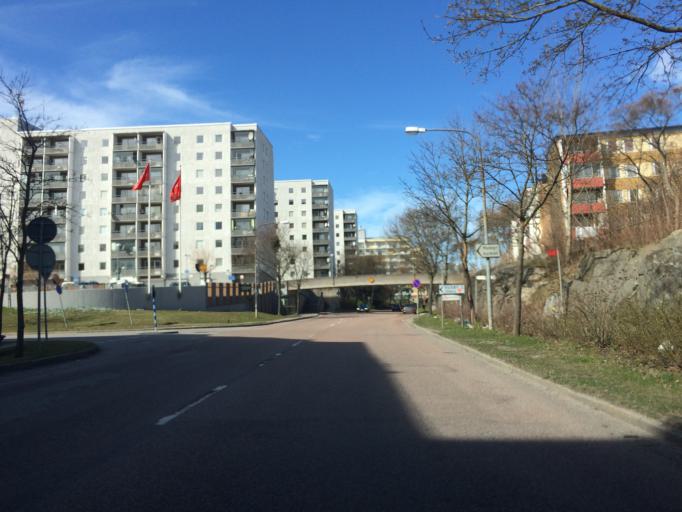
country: SE
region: Stockholm
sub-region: Stockholms Kommun
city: Kista
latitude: 59.4081
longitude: 17.9311
